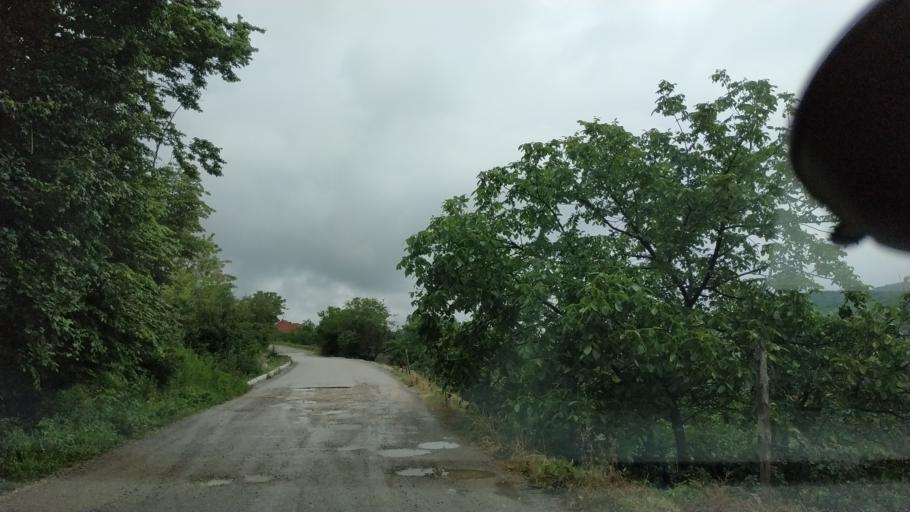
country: RS
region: Central Serbia
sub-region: Toplicki Okrug
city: Prokuplje
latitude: 43.3909
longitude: 21.5726
